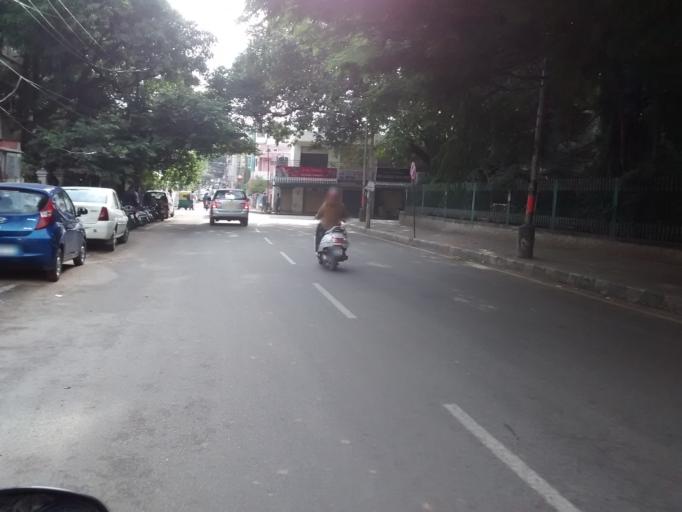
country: IN
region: Karnataka
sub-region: Bangalore Urban
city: Bangalore
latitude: 12.9437
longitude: 77.5733
